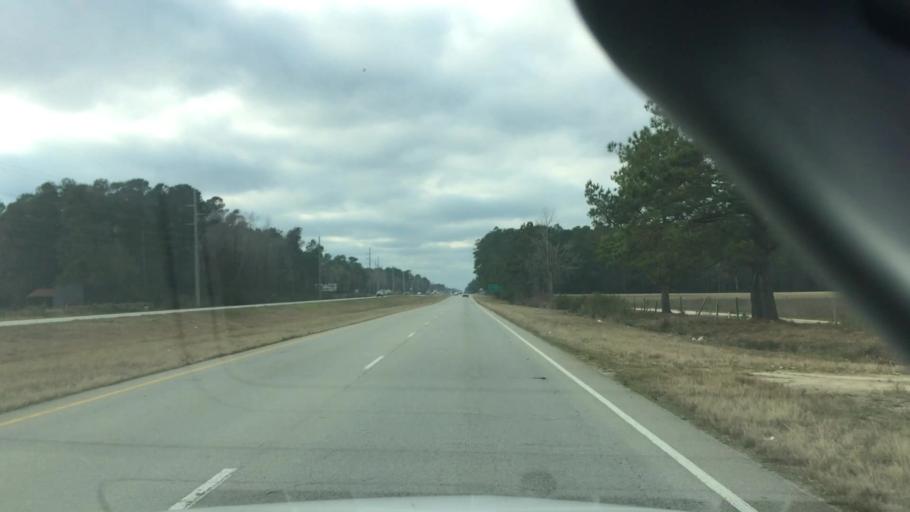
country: US
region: North Carolina
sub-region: Brunswick County
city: Shallotte
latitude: 33.9558
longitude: -78.4419
